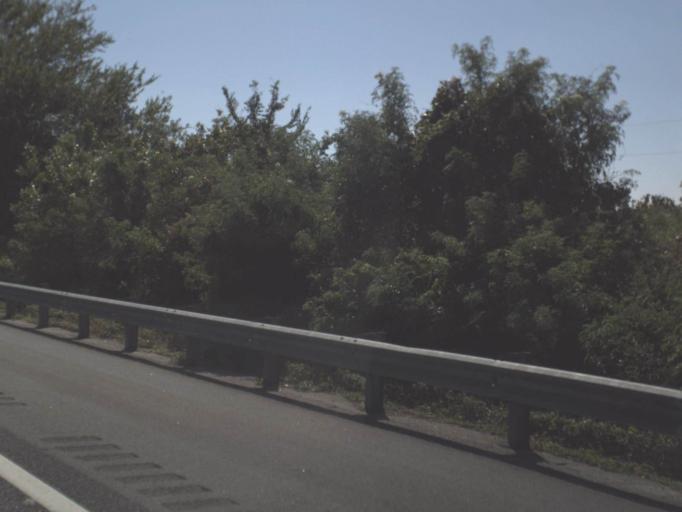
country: US
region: Florida
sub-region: Lake County
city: Hawthorne
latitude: 28.7674
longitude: -81.9516
